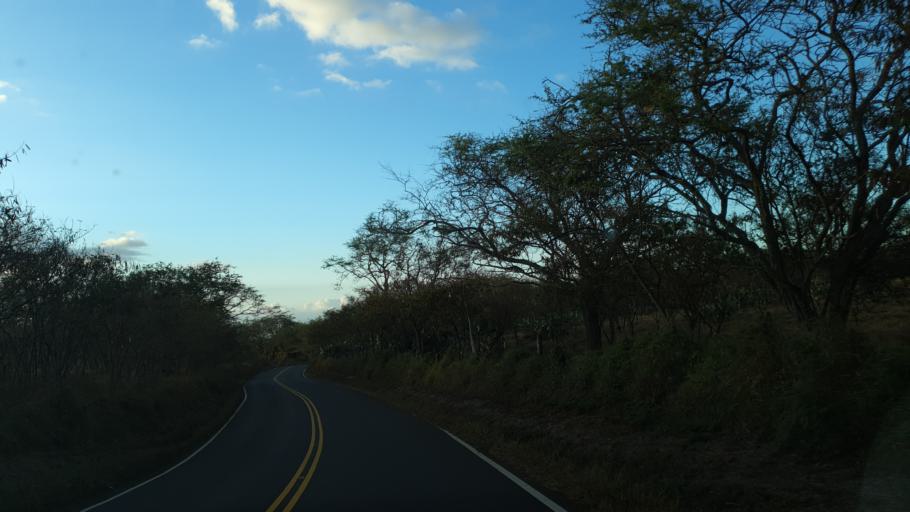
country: US
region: Hawaii
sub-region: Maui County
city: Pukalani
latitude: 20.7847
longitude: -156.3478
